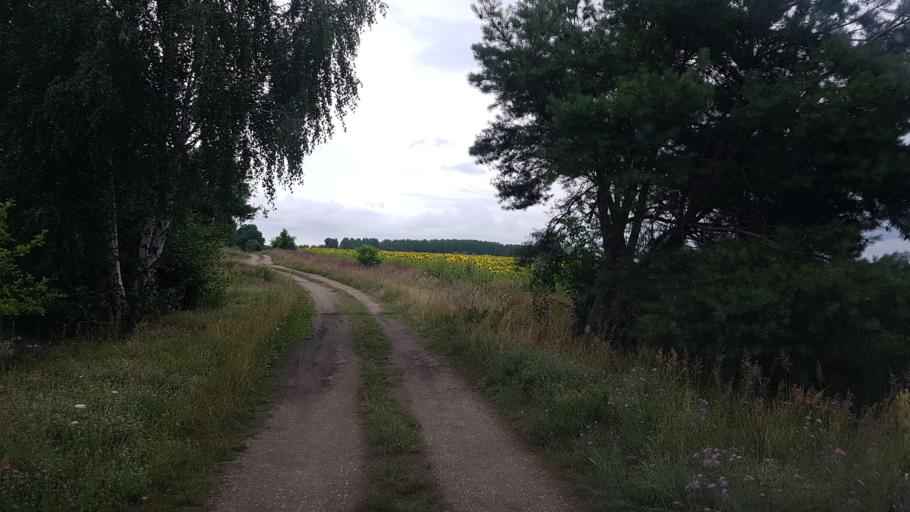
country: DE
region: Brandenburg
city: Spremberg
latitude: 51.5912
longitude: 14.3197
